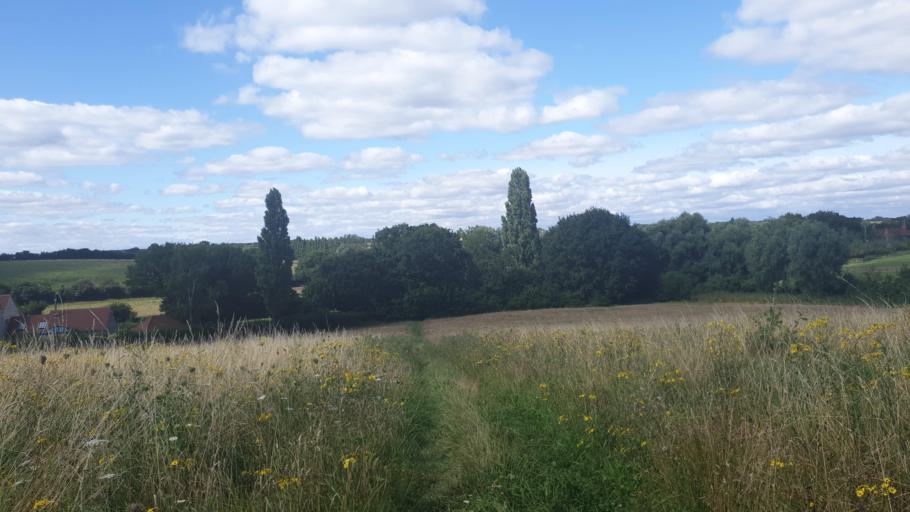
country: GB
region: England
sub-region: Suffolk
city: Shotley Gate
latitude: 51.9221
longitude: 1.2173
